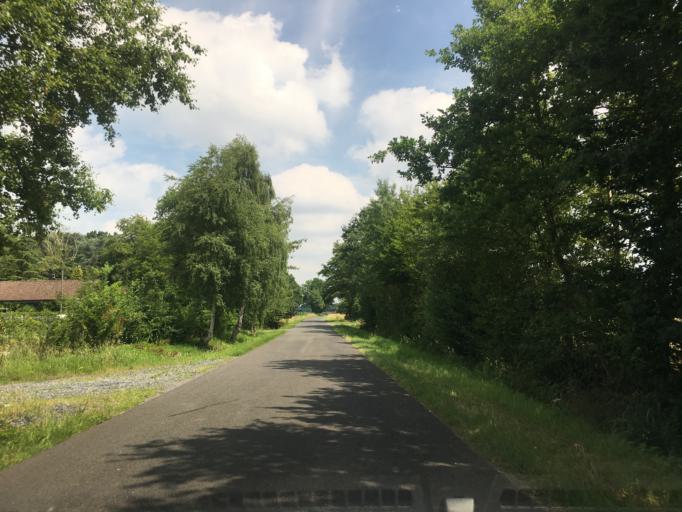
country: DE
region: North Rhine-Westphalia
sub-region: Regierungsbezirk Munster
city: Senden
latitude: 51.9227
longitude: 7.5478
